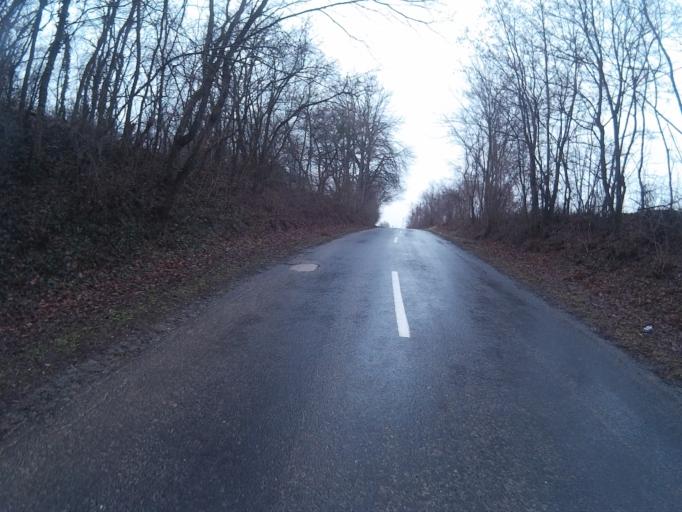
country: HU
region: Komarom-Esztergom
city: Nyergesujfalu
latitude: 47.7091
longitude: 18.5810
